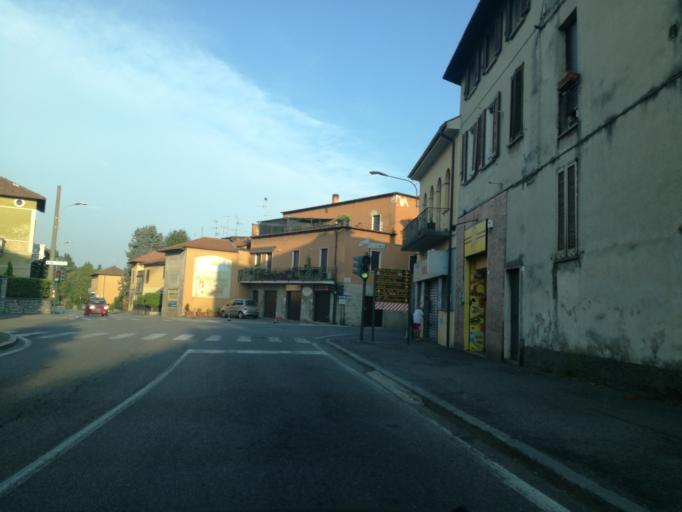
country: IT
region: Lombardy
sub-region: Provincia di Lecco
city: Paderno d'Adda
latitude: 45.6832
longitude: 9.4441
